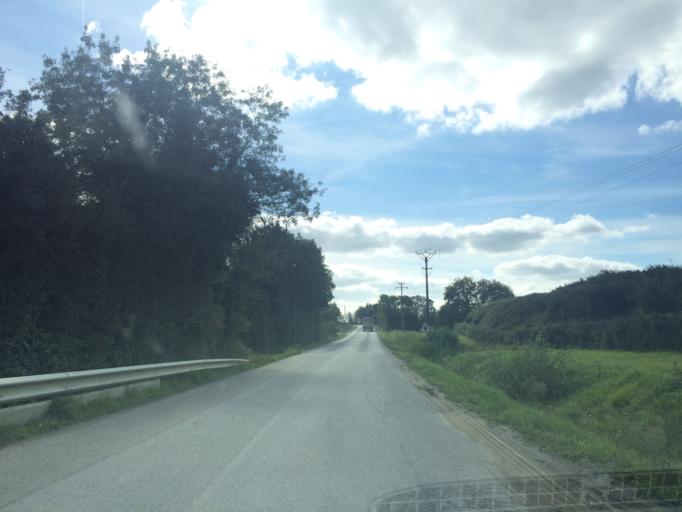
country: FR
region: Pays de la Loire
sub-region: Departement de la Loire-Atlantique
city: Rouans
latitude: 47.1658
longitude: -1.8735
